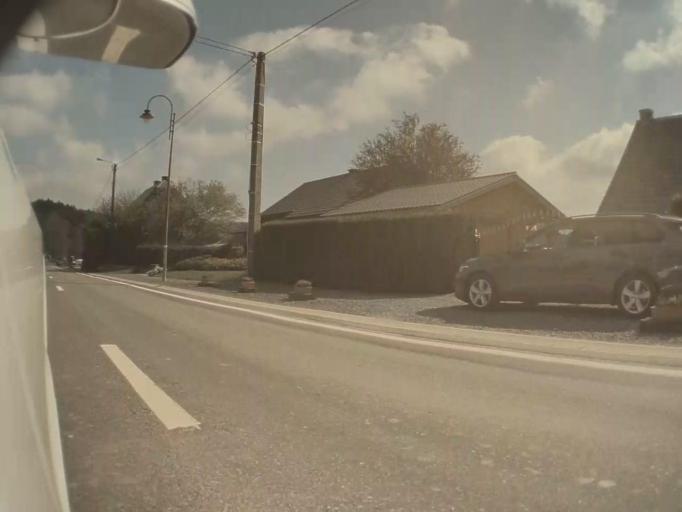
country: BE
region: Wallonia
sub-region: Province du Luxembourg
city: Tellin
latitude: 50.0866
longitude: 5.2239
